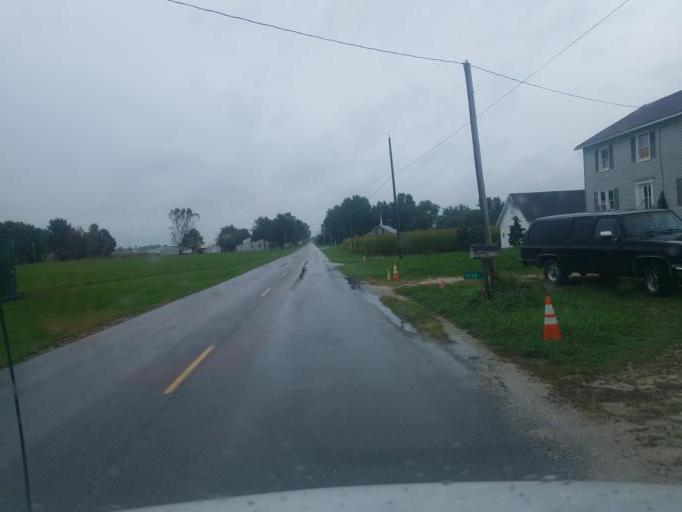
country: US
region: Ohio
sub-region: Medina County
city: Seville
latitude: 40.9840
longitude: -81.8568
